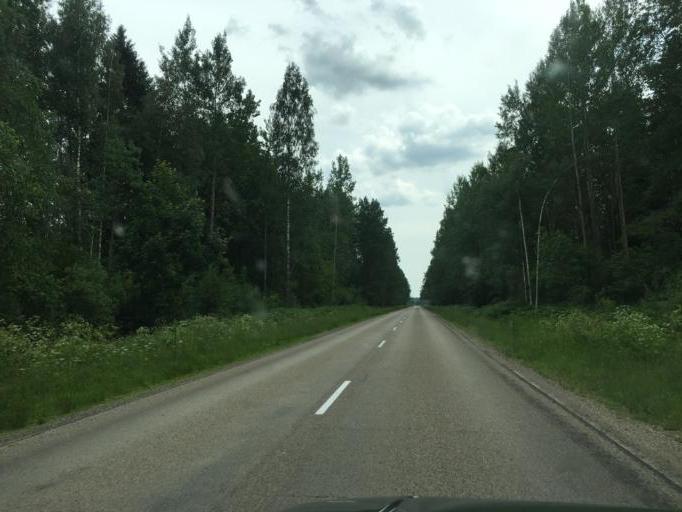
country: LV
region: Rugaju
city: Rugaji
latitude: 56.8195
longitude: 27.0949
